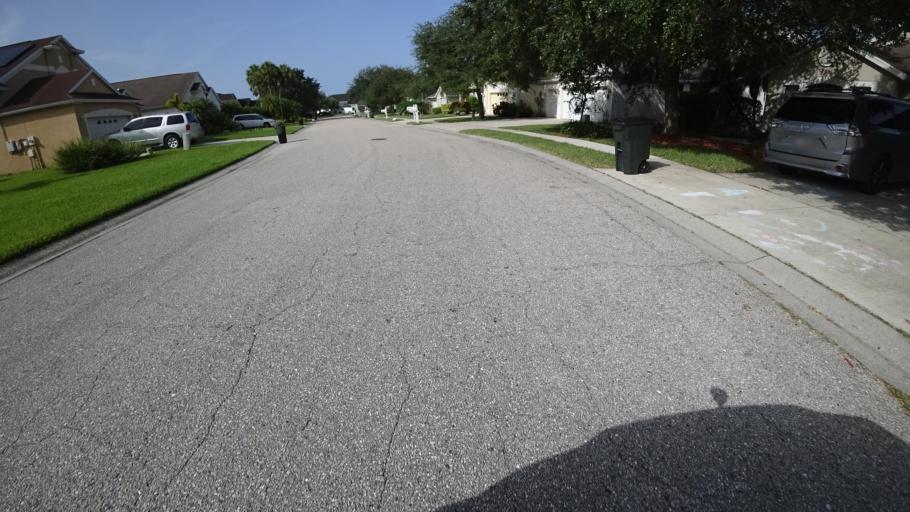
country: US
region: Florida
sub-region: Manatee County
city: Ellenton
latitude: 27.5510
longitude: -82.4982
